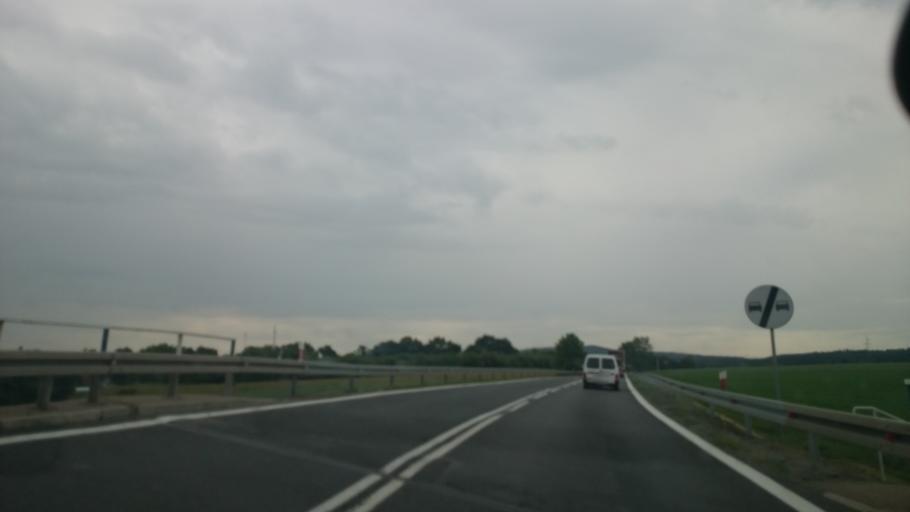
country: PL
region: Lower Silesian Voivodeship
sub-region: Powiat dzierzoniowski
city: Niemcza
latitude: 50.7321
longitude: 16.8358
